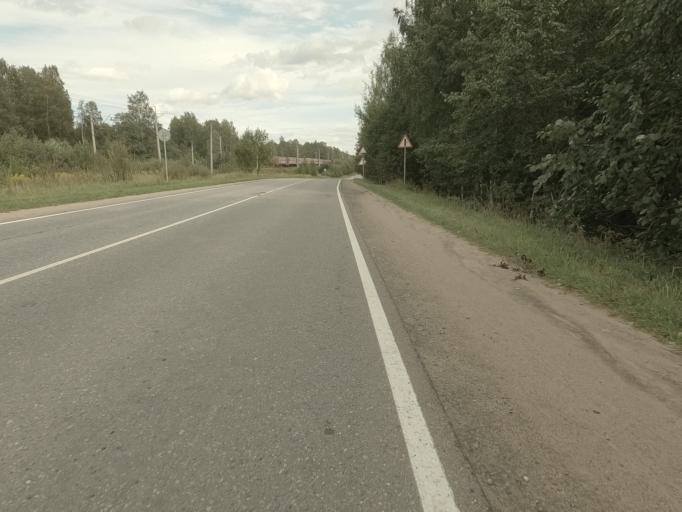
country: RU
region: Leningrad
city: Mga
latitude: 59.7623
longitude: 30.9927
